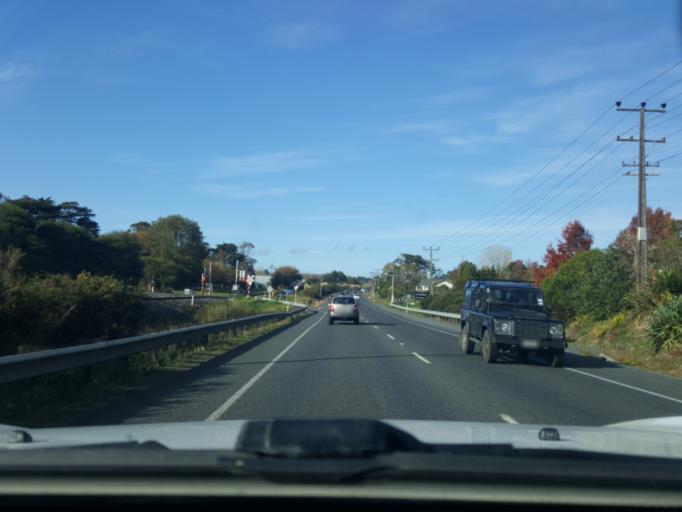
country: NZ
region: Auckland
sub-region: Auckland
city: Muriwai Beach
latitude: -36.7665
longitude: 174.5021
